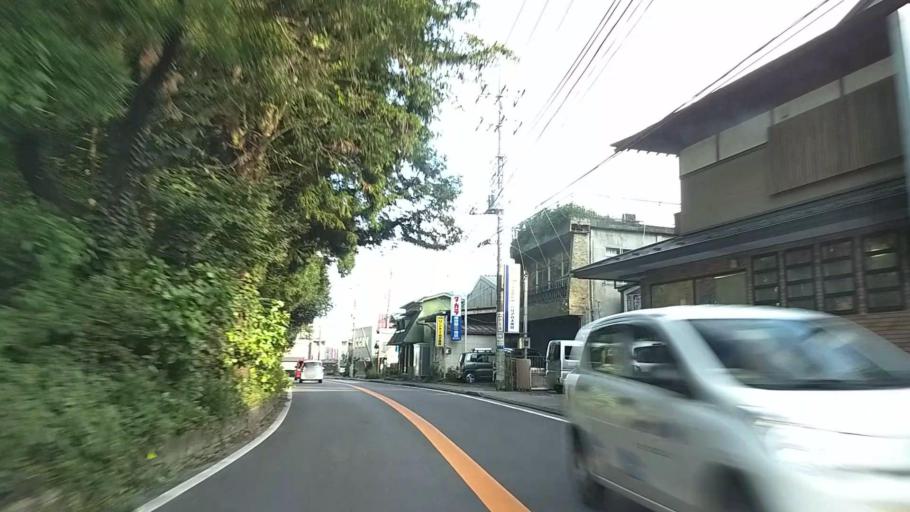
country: JP
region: Tochigi
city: Imaichi
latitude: 36.7230
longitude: 139.6904
